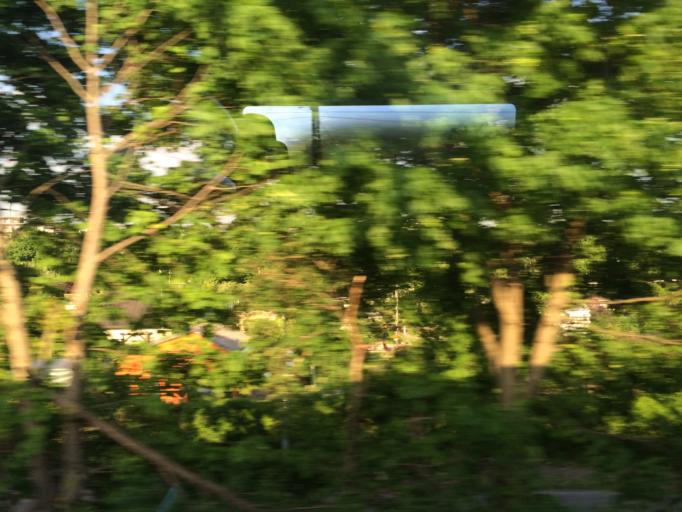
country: DE
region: North Rhine-Westphalia
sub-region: Regierungsbezirk Dusseldorf
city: Hochfeld
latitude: 51.4046
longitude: 6.7731
